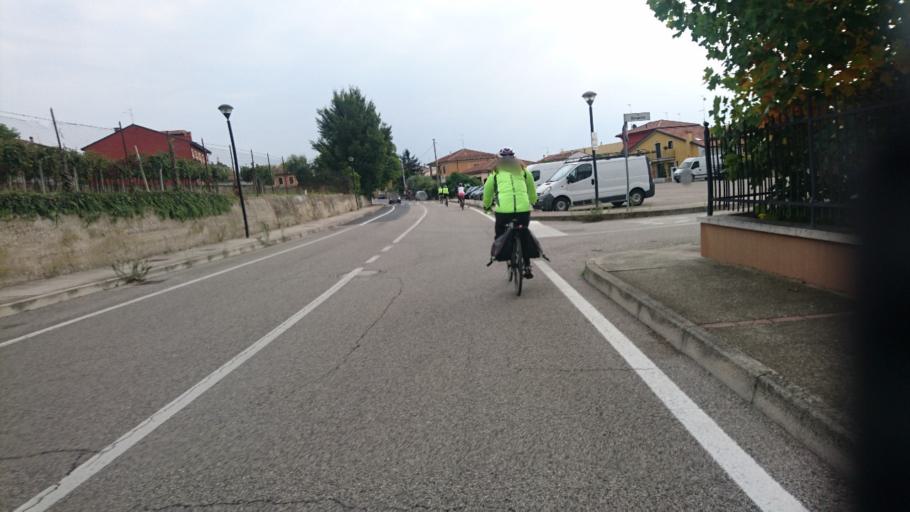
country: IT
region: Veneto
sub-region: Provincia di Verona
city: Caldiero
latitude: 45.4089
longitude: 11.1786
